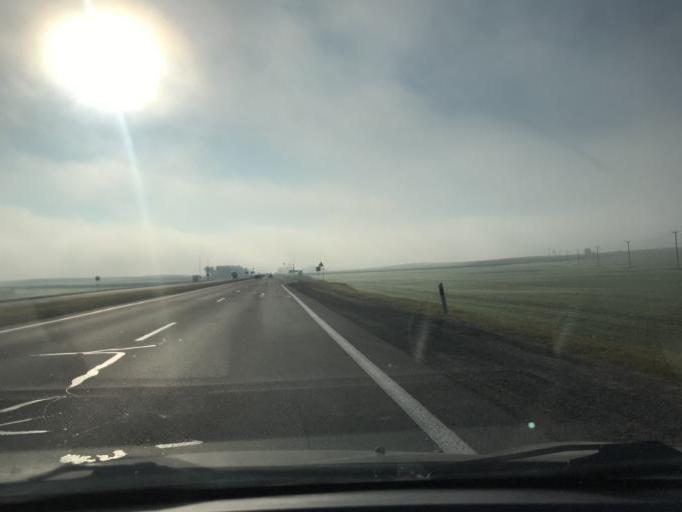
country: BY
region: Minsk
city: Luhavaya Slabada
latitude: 53.7377
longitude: 27.8456
